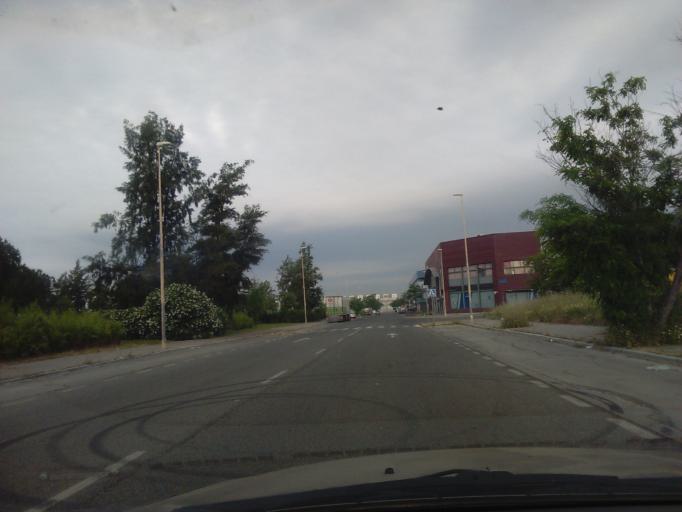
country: ES
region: Andalusia
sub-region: Provincia de Sevilla
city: Sevilla
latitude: 37.3803
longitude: -5.9287
